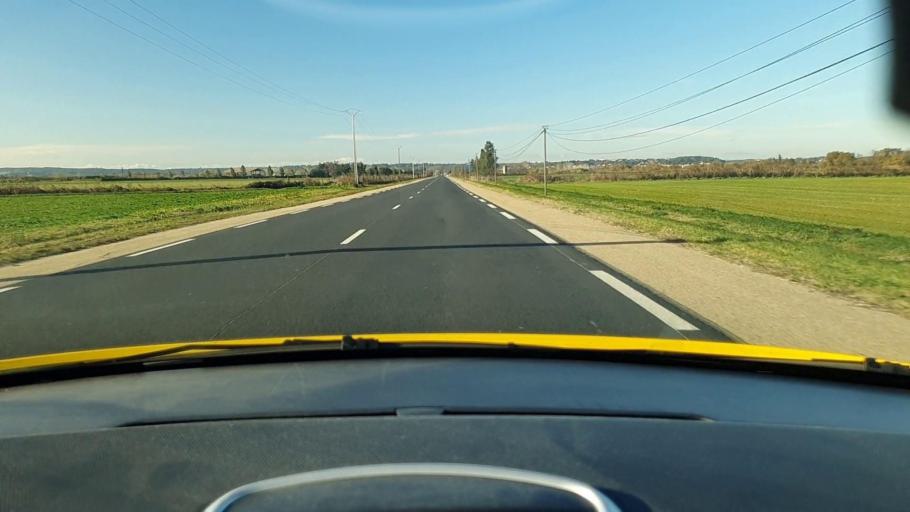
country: FR
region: Languedoc-Roussillon
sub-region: Departement du Gard
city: Bellegarde
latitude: 43.7258
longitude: 4.5398
